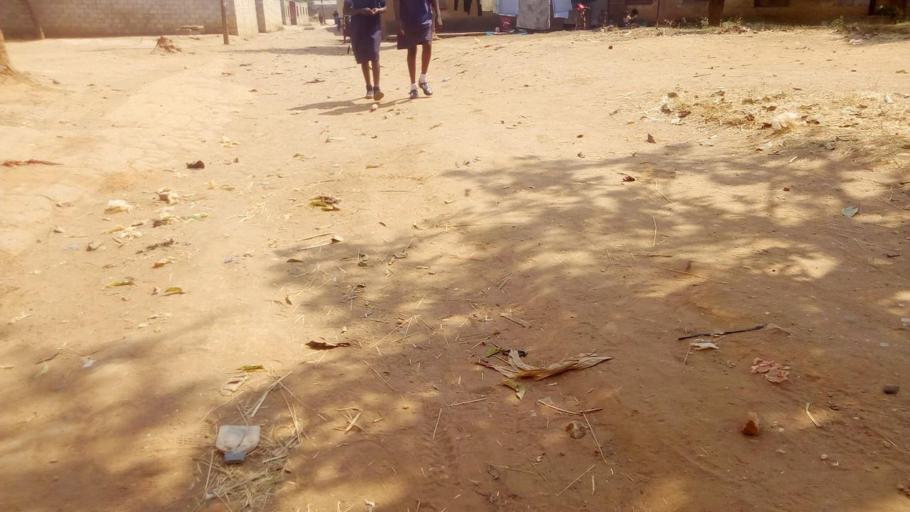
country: ZM
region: Lusaka
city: Lusaka
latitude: -15.3576
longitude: 28.2975
